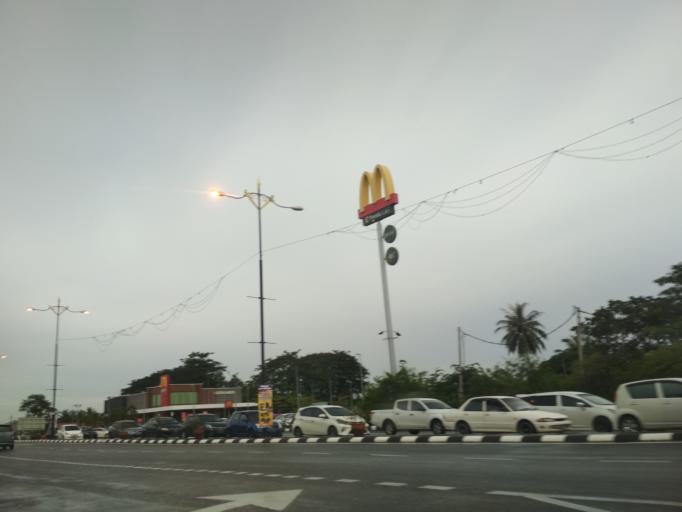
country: MY
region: Perlis
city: Kangar
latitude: 6.4330
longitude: 100.1956
